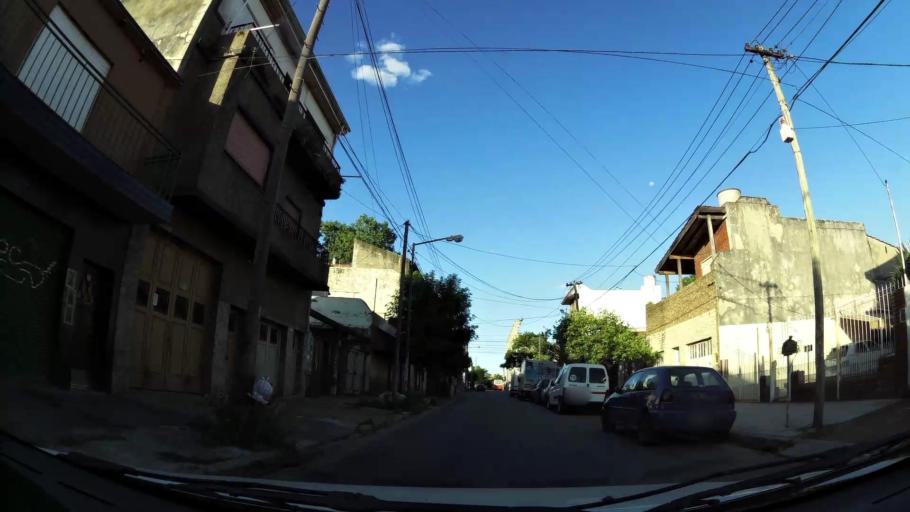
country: AR
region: Buenos Aires
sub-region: Partido de General San Martin
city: General San Martin
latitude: -34.5680
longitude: -58.5299
